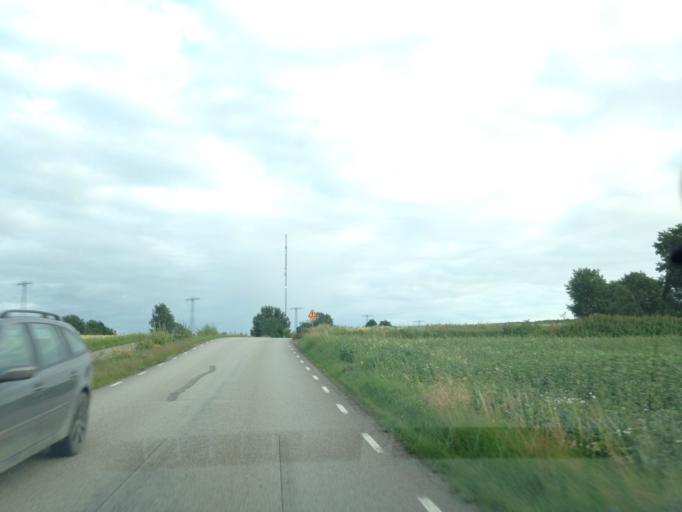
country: SE
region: Halland
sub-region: Varbergs Kommun
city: Tvaaker
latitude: 57.1210
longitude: 12.3916
